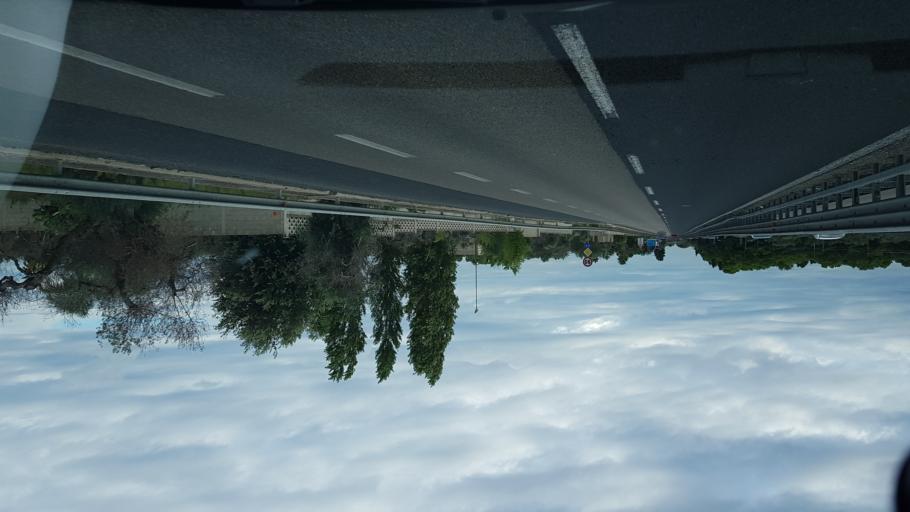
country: IT
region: Apulia
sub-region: Provincia di Lecce
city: Cavallino
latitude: 40.3007
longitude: 18.1934
